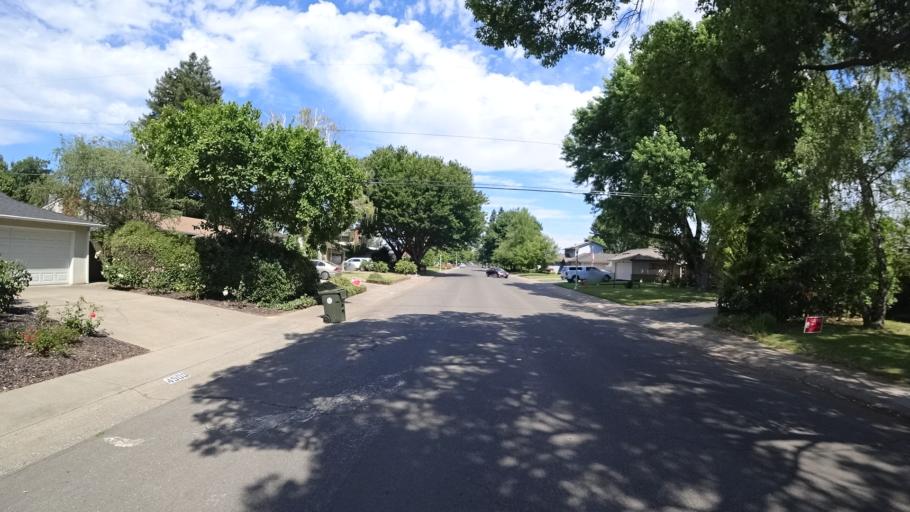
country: US
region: California
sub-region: Sacramento County
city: Sacramento
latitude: 38.5826
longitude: -121.4431
